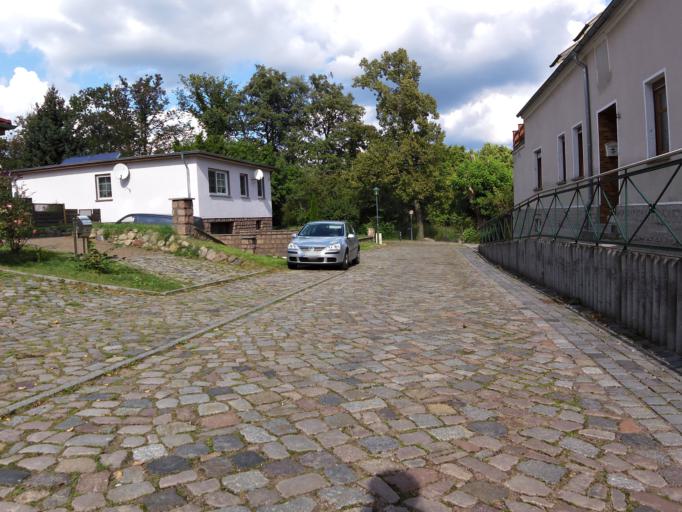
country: DE
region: Saxony-Anhalt
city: Worlitz
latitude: 51.8446
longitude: 12.4249
